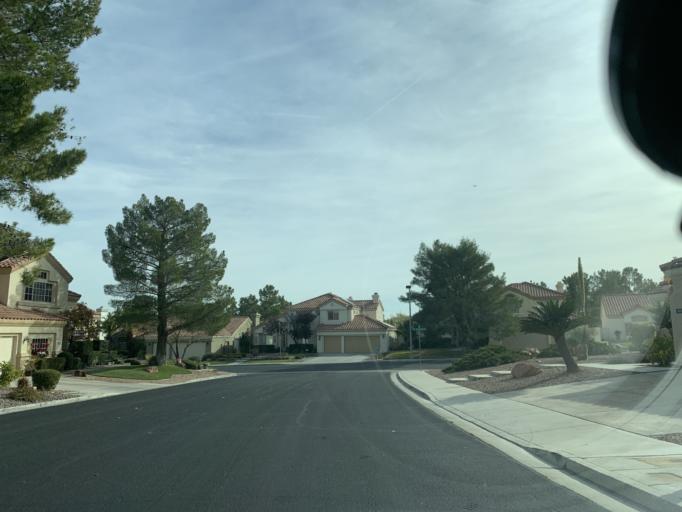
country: US
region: Nevada
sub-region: Clark County
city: Summerlin South
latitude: 36.1516
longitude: -115.3001
